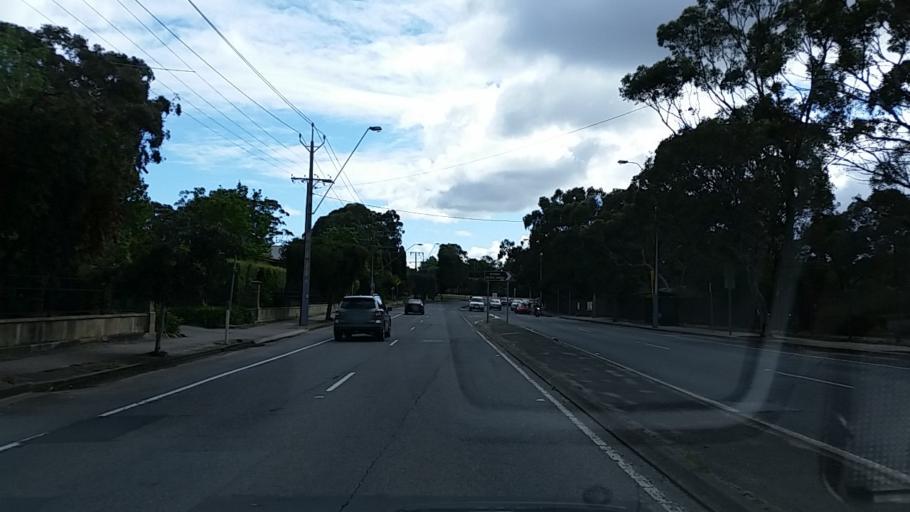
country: AU
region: South Australia
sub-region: Mitcham
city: Blackwood
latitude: -35.0227
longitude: 138.6079
